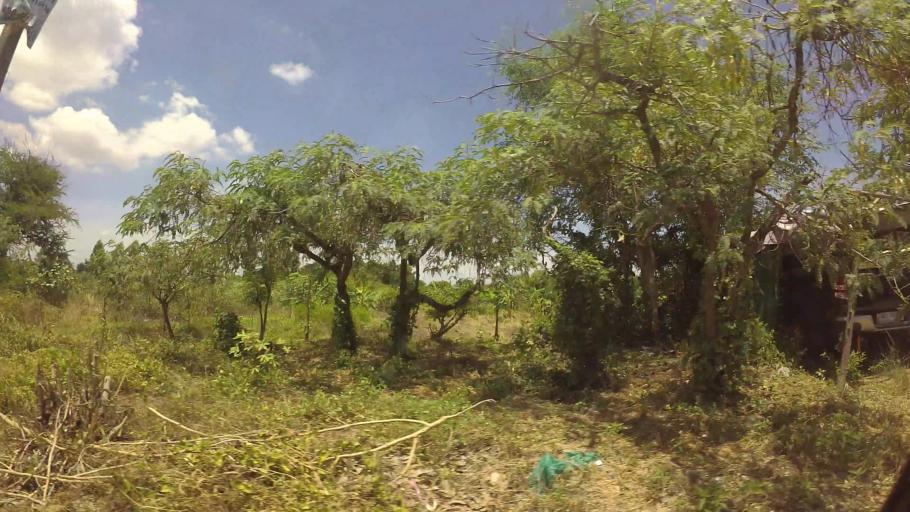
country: TH
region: Chon Buri
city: Si Racha
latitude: 13.1175
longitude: 100.9426
